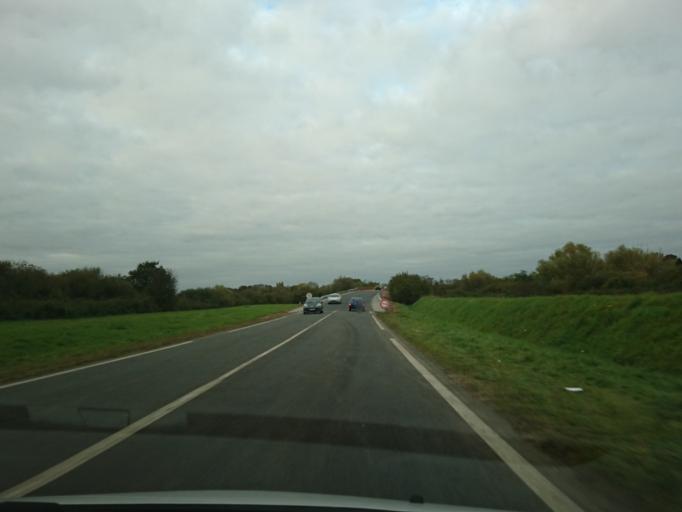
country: FR
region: Pays de la Loire
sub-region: Departement de la Loire-Atlantique
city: Indre
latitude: 47.2042
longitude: -1.6670
